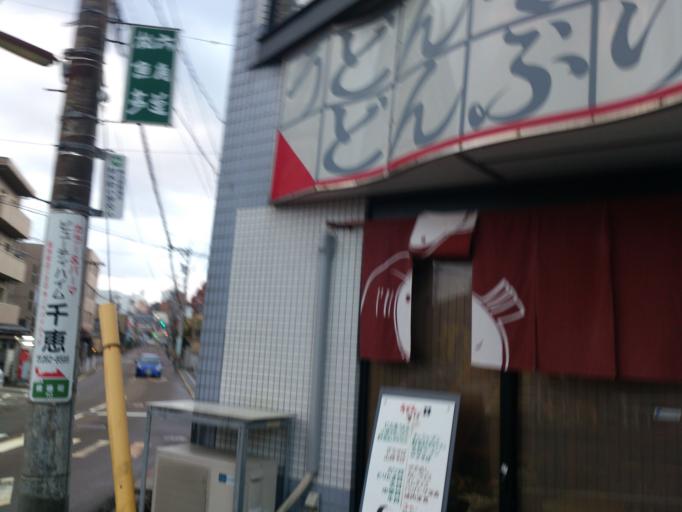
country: JP
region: Ishikawa
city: Kanazawa-shi
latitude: 36.5692
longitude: 136.6682
